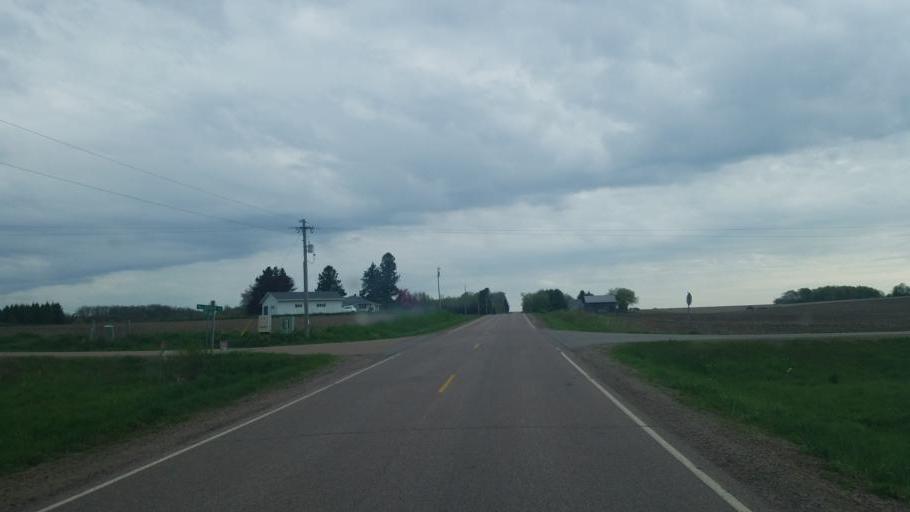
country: US
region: Wisconsin
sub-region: Wood County
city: Marshfield
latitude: 44.5843
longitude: -90.2994
